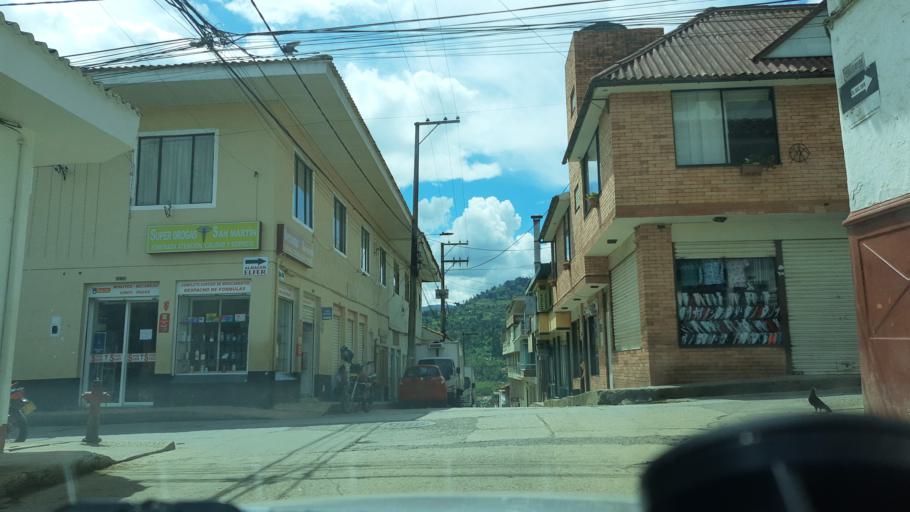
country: CO
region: Boyaca
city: Guateque
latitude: 5.0075
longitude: -73.4723
